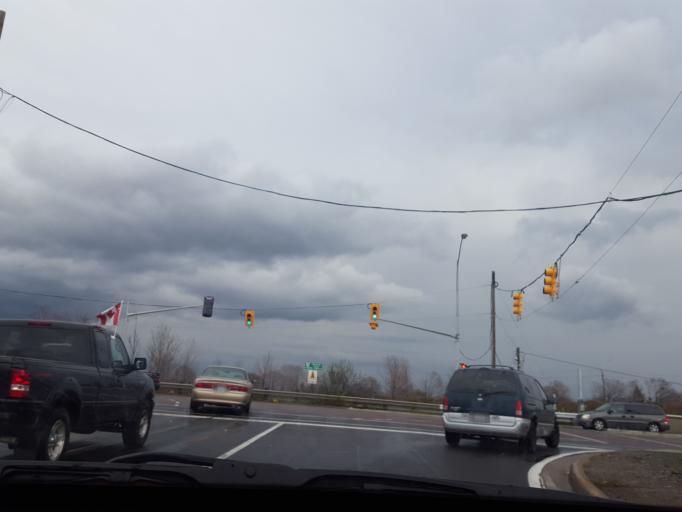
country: CA
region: Ontario
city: Pickering
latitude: 43.8148
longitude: -79.1142
